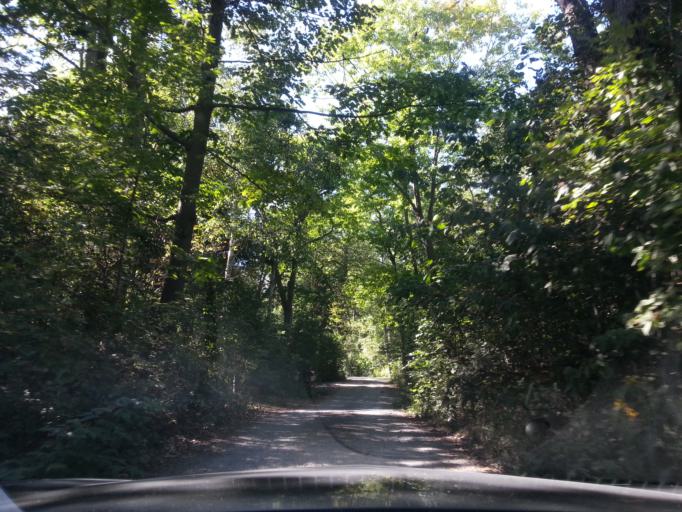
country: CA
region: Ontario
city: Prince Edward
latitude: 43.9037
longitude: -77.2304
